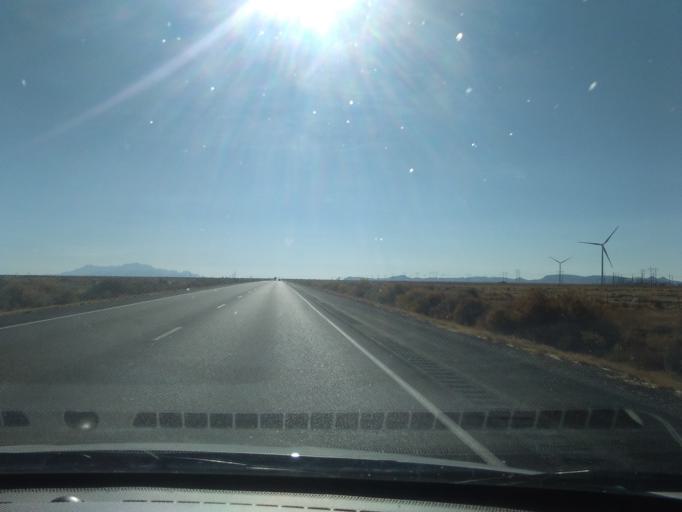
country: US
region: New Mexico
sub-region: Dona Ana County
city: Hatch
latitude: 32.5439
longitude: -107.4812
